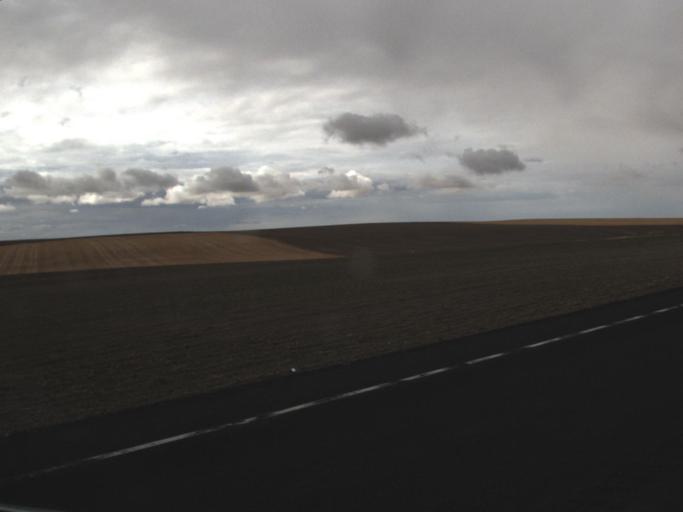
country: US
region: Washington
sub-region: Okanogan County
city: Coulee Dam
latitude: 47.6945
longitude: -118.9666
